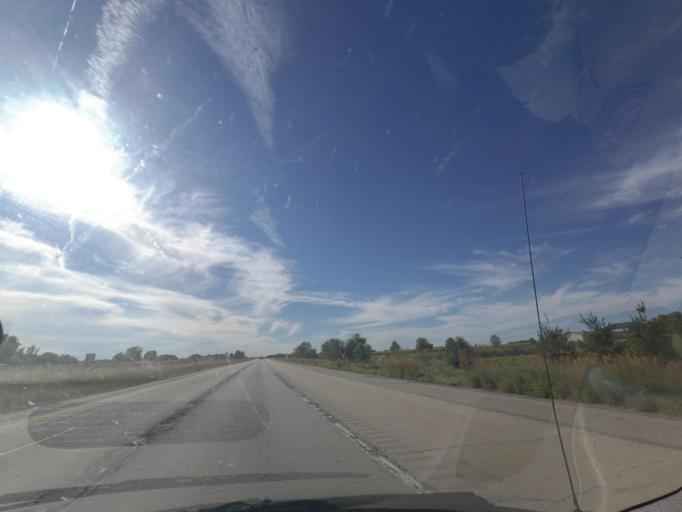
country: US
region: Illinois
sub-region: Macon County
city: Forsyth
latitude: 39.9079
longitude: -88.9765
